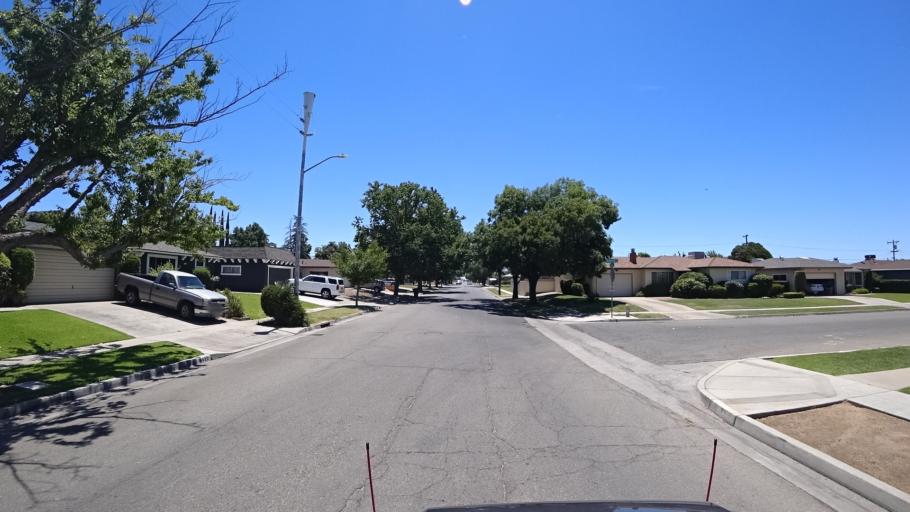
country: US
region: California
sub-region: Fresno County
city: Tarpey Village
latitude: 36.7982
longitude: -119.7498
